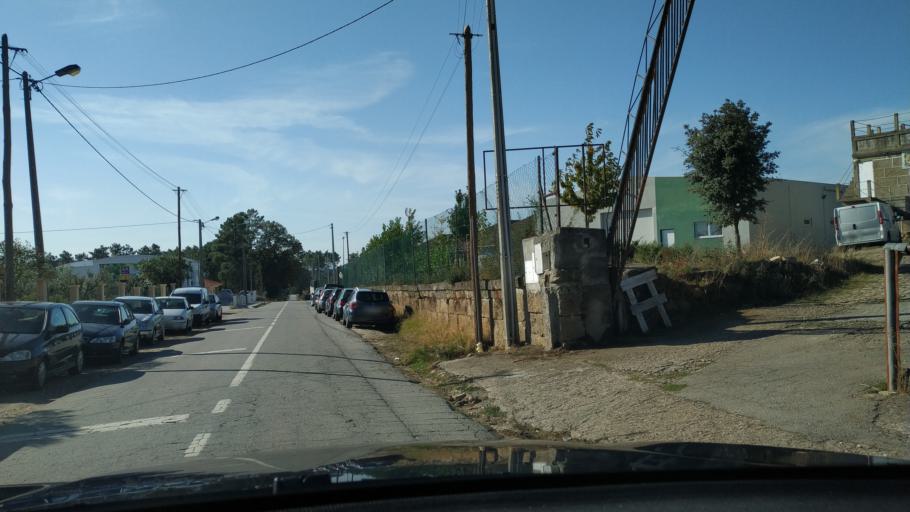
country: PT
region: Vila Real
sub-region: Sabrosa
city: Vilela
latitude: 41.2622
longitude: -7.6211
